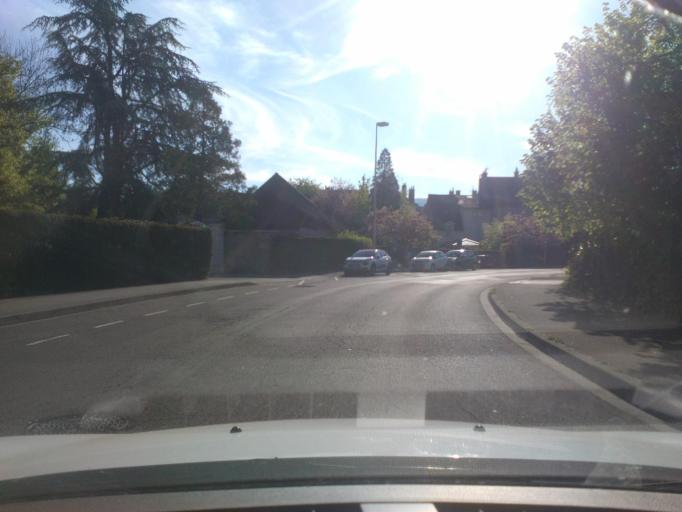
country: FR
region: Franche-Comte
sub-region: Departement du Jura
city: Lons-le-Saunier
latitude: 46.6779
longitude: 5.5524
